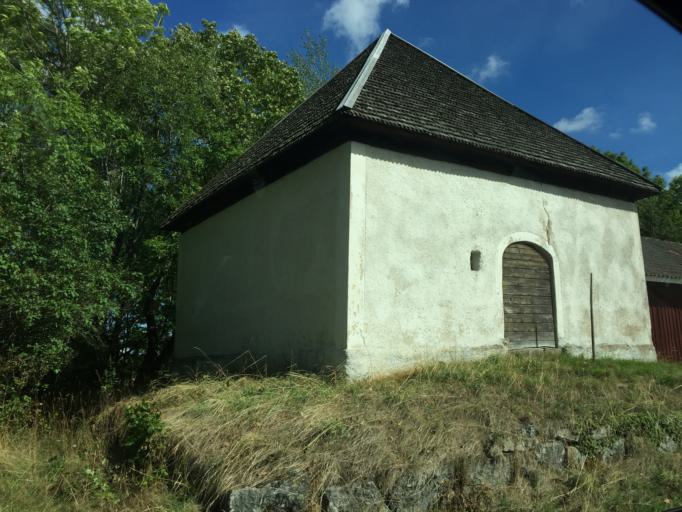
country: SE
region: OErebro
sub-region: Hallsbergs Kommun
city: Hallsberg
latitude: 59.1040
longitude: 15.0067
